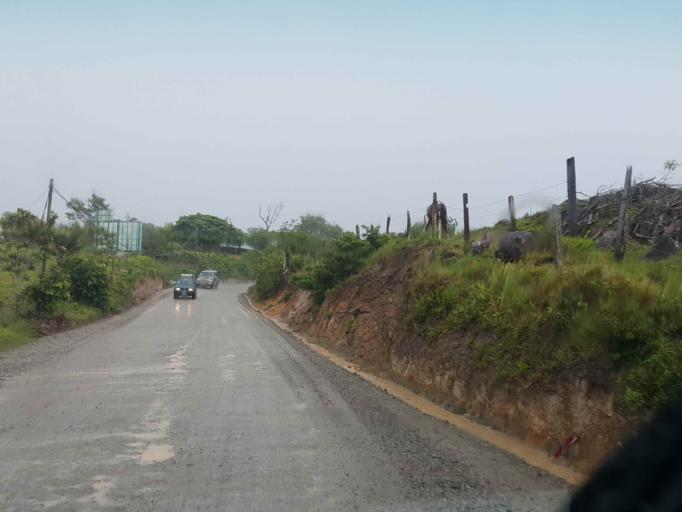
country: CR
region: Guanacaste
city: Juntas
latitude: 10.2339
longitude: -84.8528
